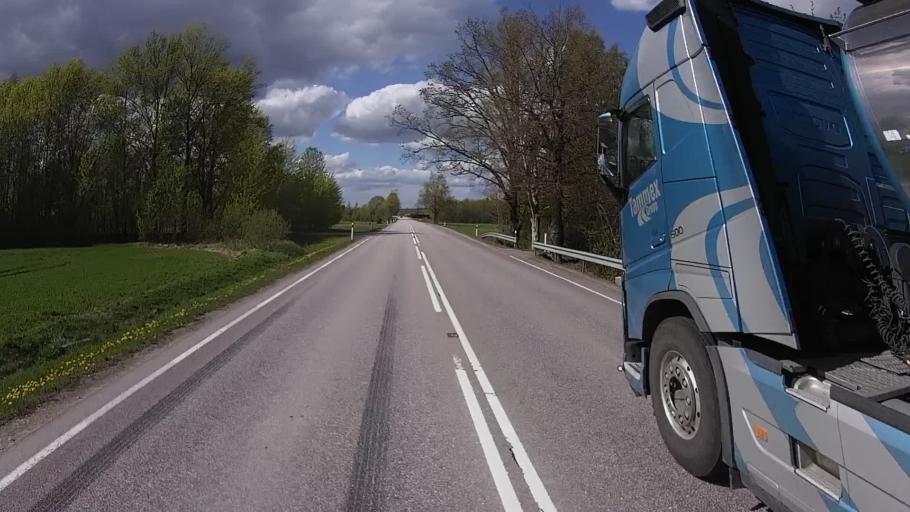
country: EE
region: Jogevamaa
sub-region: Jogeva linn
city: Jogeva
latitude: 58.6746
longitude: 26.4911
